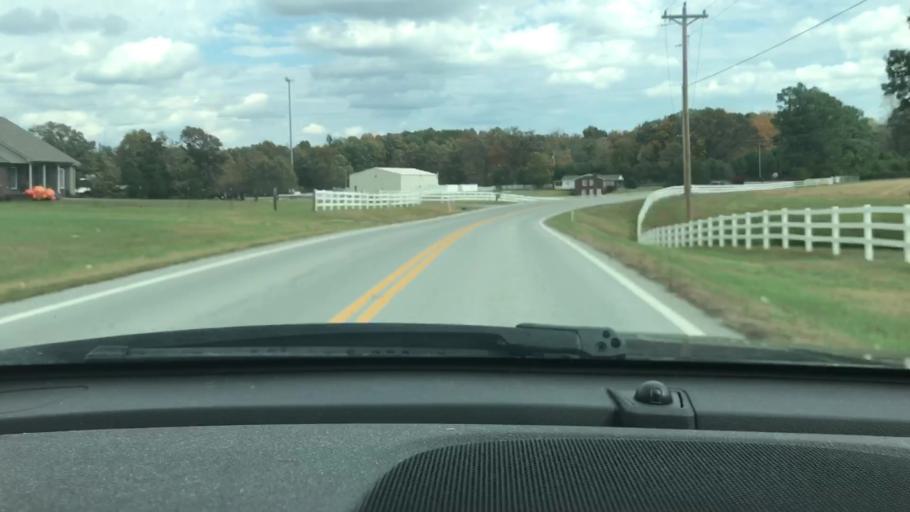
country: US
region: Tennessee
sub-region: Dickson County
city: Charlotte
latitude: 36.2137
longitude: -87.2701
